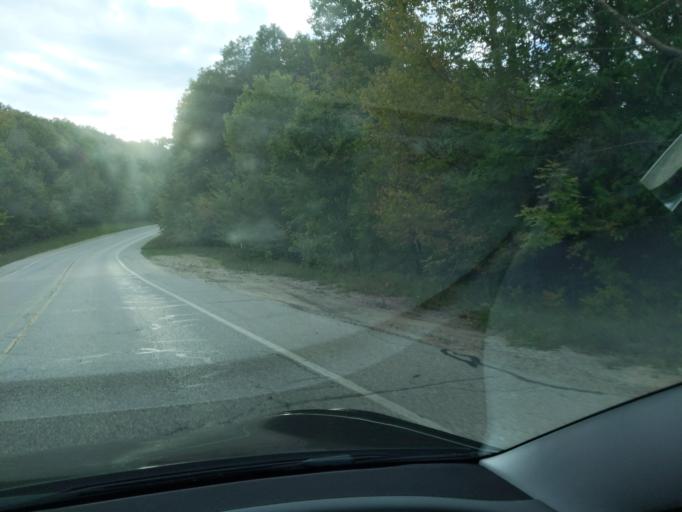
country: US
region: Michigan
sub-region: Kalkaska County
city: Rapid City
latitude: 44.7807
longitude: -85.2748
